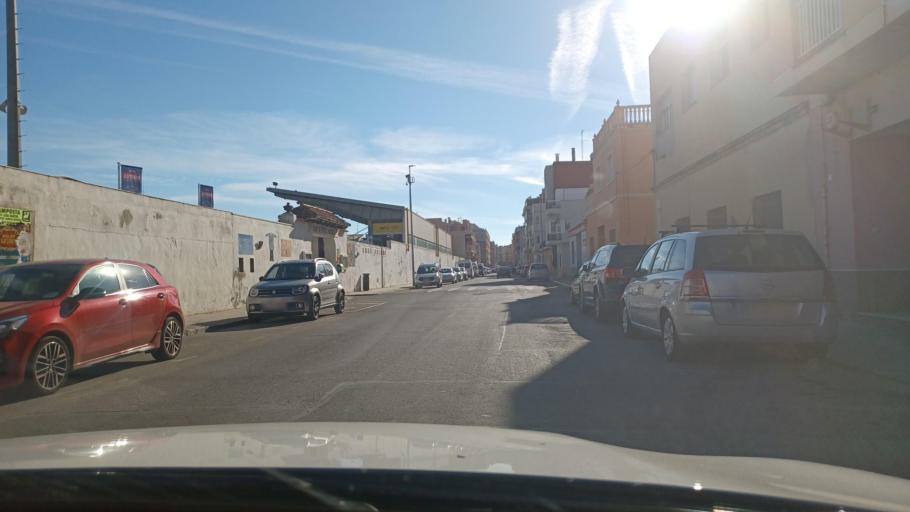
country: ES
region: Catalonia
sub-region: Provincia de Tarragona
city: Amposta
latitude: 40.7082
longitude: 0.5807
